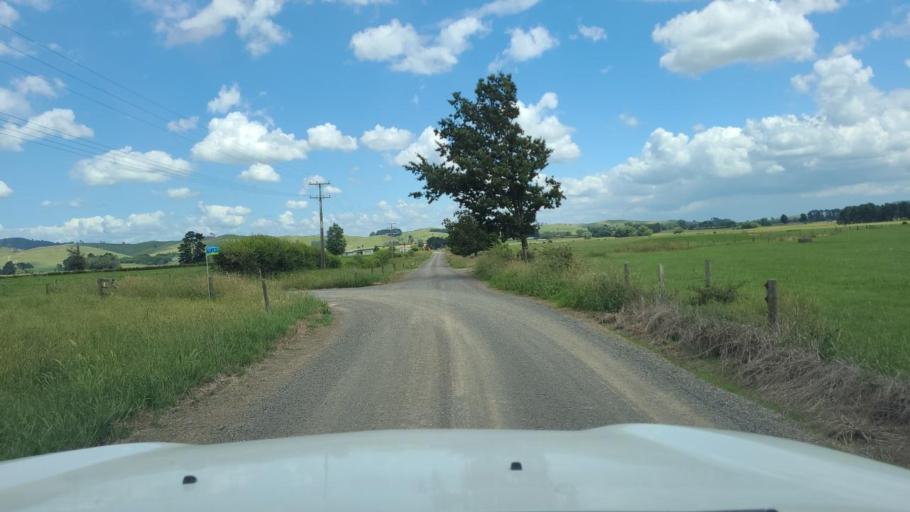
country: NZ
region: Waikato
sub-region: Hauraki District
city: Ngatea
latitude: -37.5242
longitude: 175.4129
